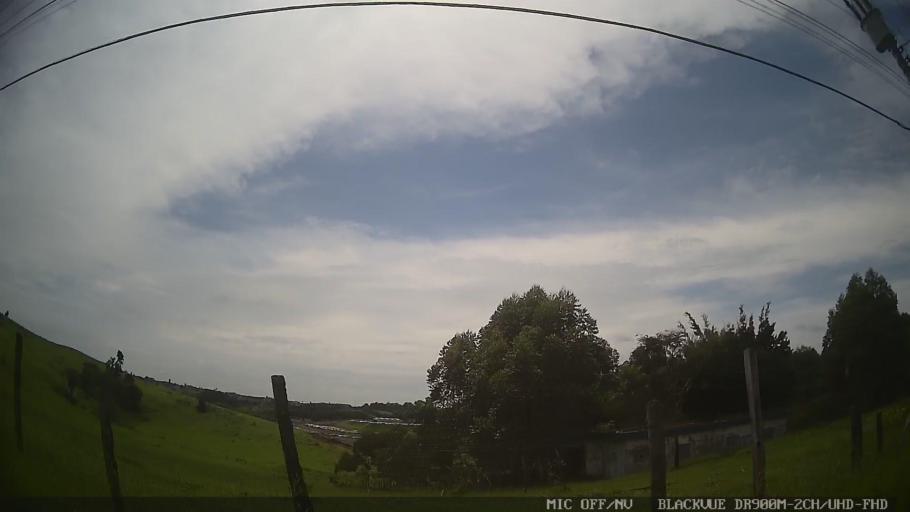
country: BR
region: Sao Paulo
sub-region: Santa Isabel
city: Santa Isabel
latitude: -23.3675
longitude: -46.1796
